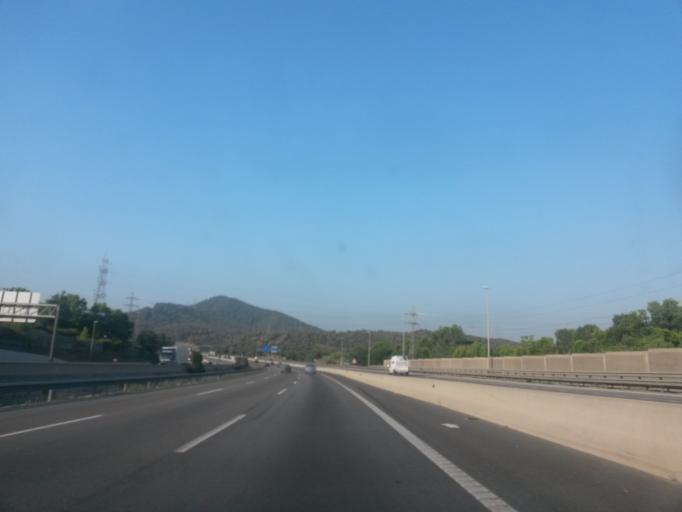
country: ES
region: Catalonia
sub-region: Provincia de Barcelona
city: Rubi
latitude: 41.4720
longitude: 2.0359
